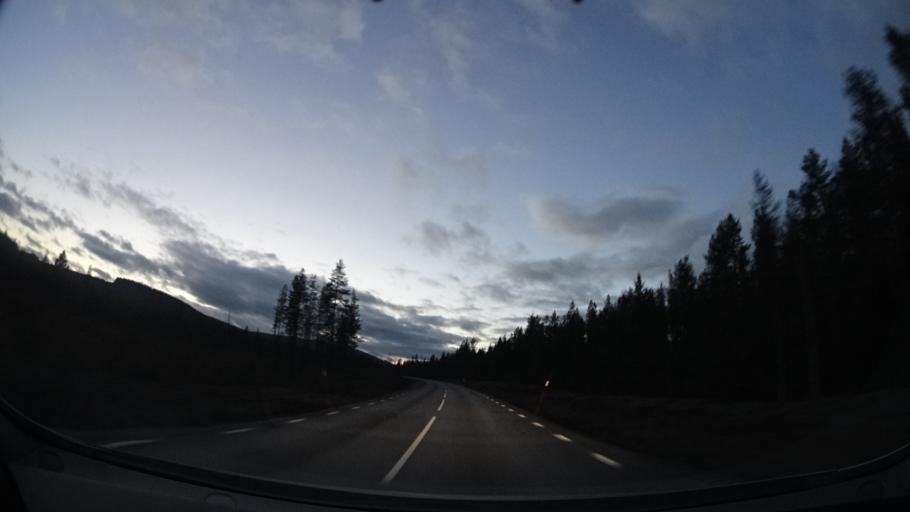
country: SE
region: Vaesterbotten
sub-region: Asele Kommun
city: Asele
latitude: 64.2011
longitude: 17.0523
